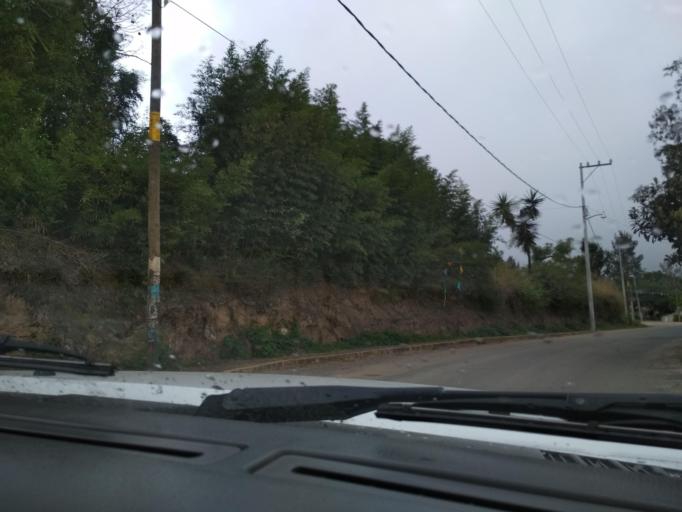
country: MX
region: Veracruz
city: El Castillo
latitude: 19.5417
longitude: -96.8256
